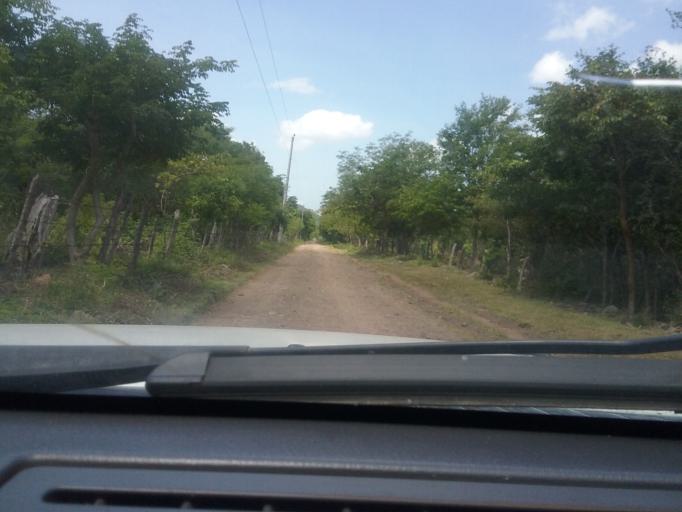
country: NI
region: Matagalpa
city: Terrabona
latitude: 12.6579
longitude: -85.9898
